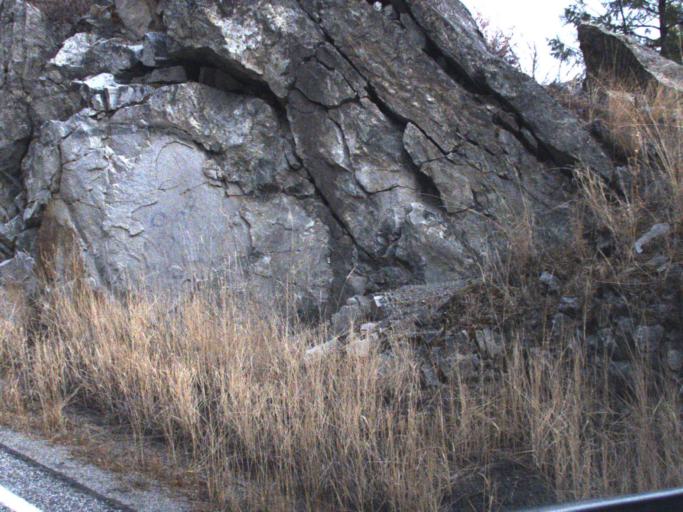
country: CA
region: British Columbia
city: Grand Forks
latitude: 48.8727
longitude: -118.2130
